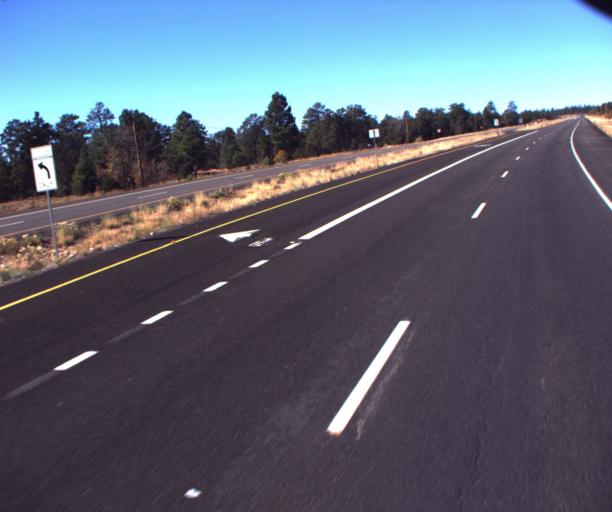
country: US
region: Arizona
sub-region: Apache County
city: Saint Michaels
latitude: 35.6586
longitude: -109.1564
